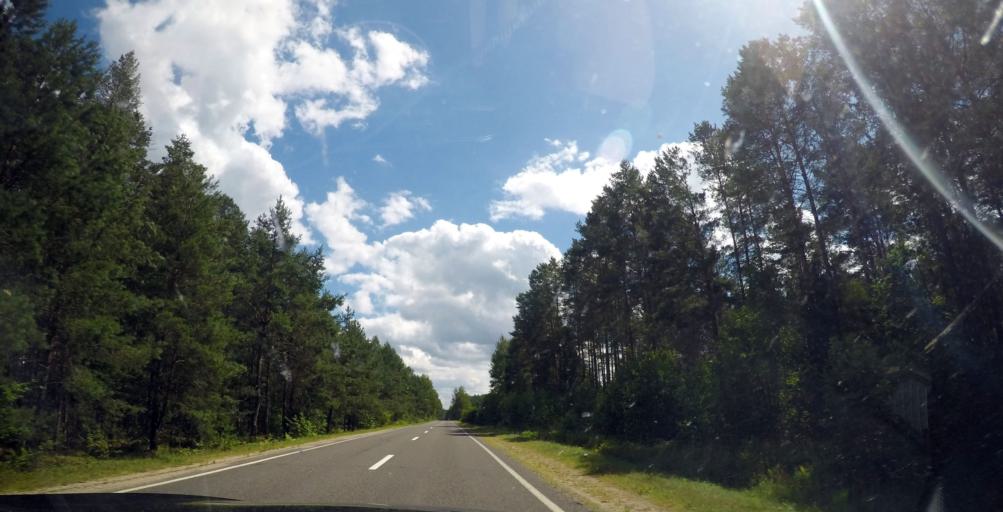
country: LT
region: Alytaus apskritis
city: Druskininkai
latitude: 53.8752
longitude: 24.1507
